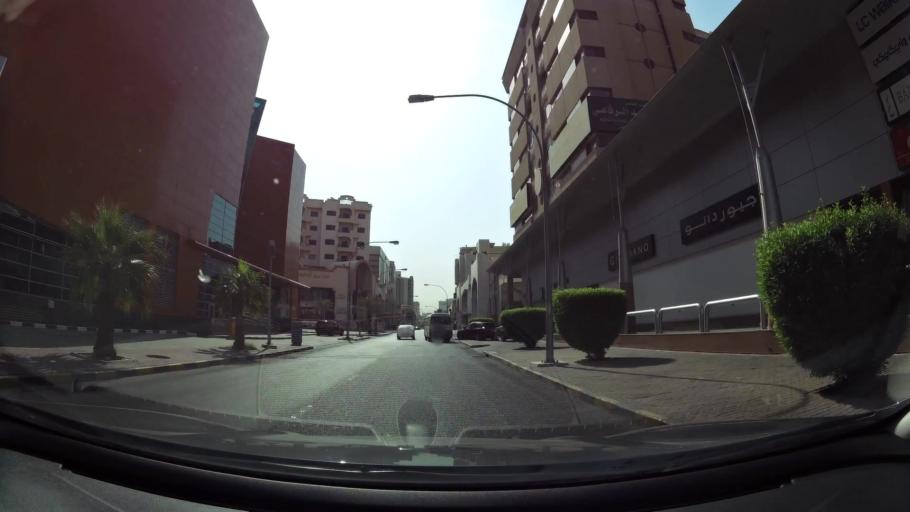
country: KW
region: Al Asimah
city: Ad Dasmah
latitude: 29.3464
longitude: 48.0113
